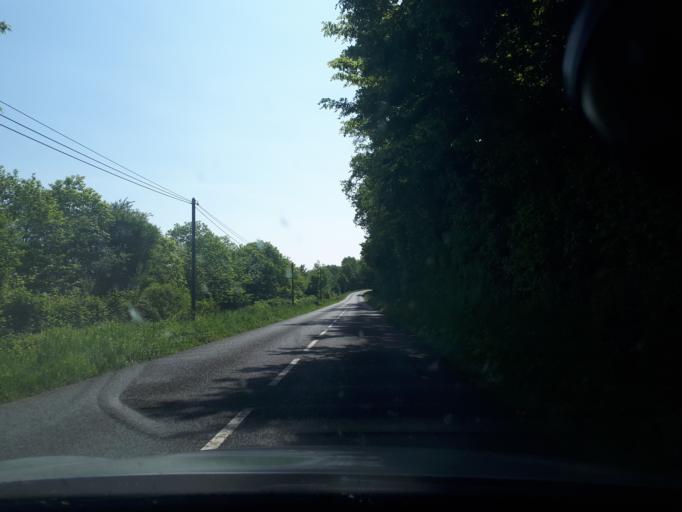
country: FR
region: Pays de la Loire
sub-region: Departement de la Sarthe
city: Champagne
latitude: 48.0749
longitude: 0.3351
